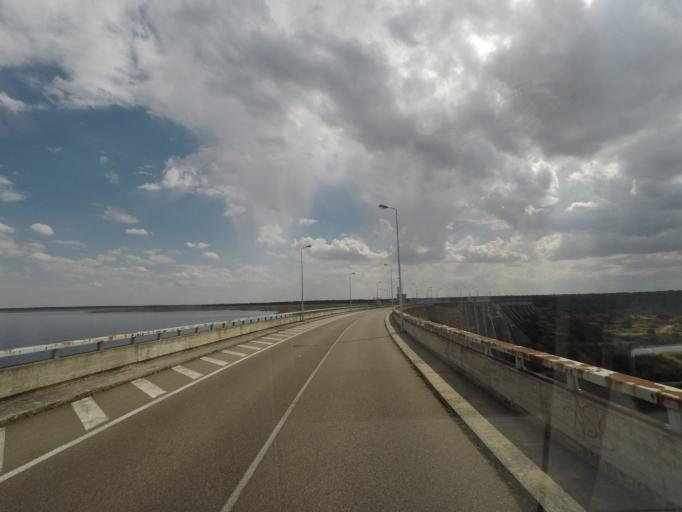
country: ES
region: Castille and Leon
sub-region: Provincia de Salamanca
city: Almendra
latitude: 41.2709
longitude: -6.3200
